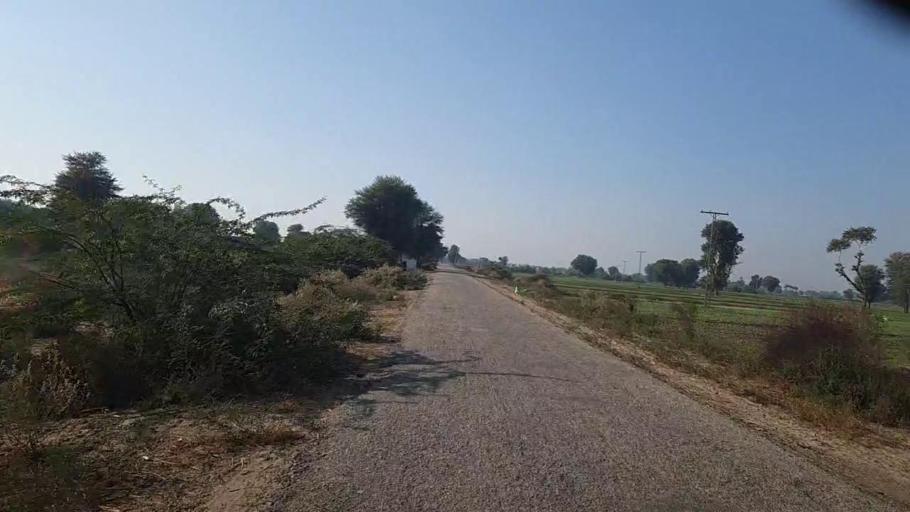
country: PK
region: Sindh
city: Darya Khan Marri
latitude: 26.6847
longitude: 68.3560
